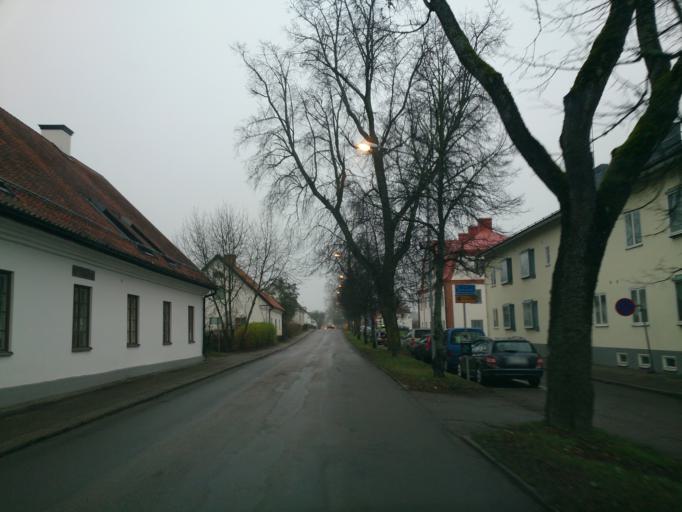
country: SE
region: OEstergoetland
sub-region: Atvidabergs Kommun
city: Atvidaberg
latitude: 58.2010
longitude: 15.9974
